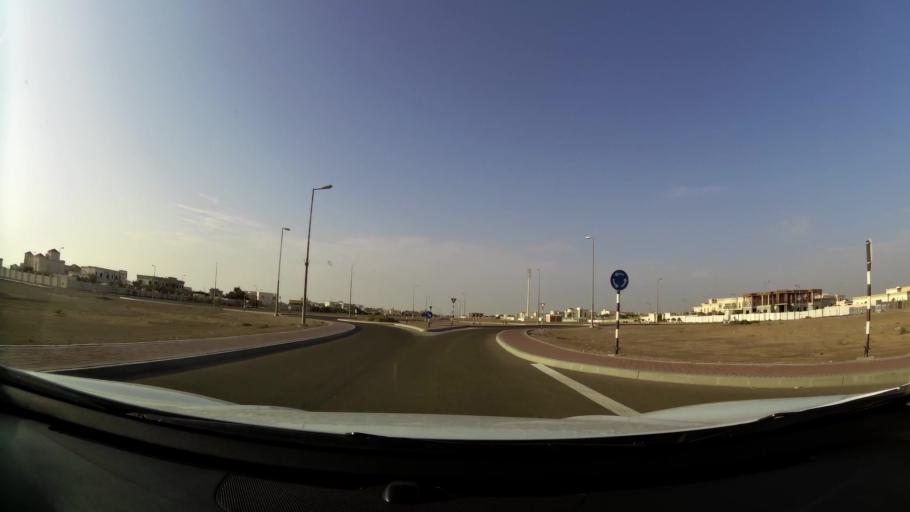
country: AE
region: Abu Dhabi
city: Al Ain
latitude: 24.0999
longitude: 55.8352
